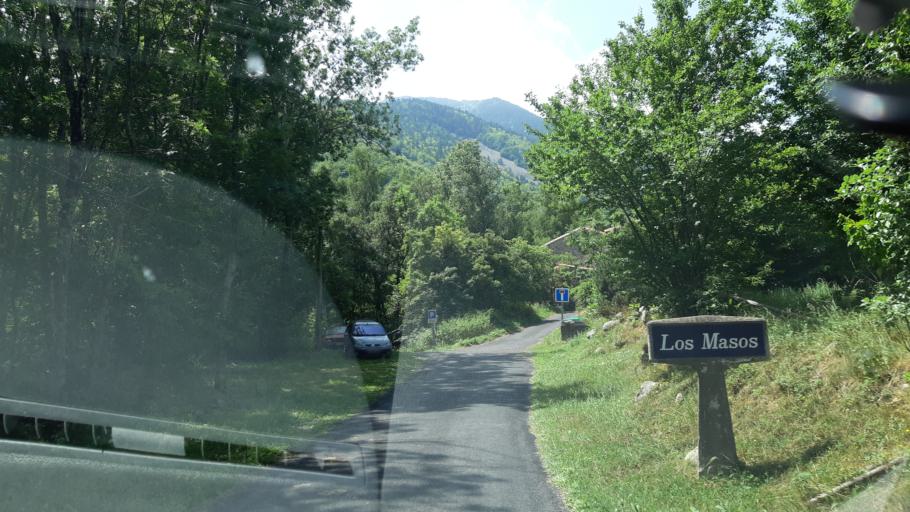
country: FR
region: Languedoc-Roussillon
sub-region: Departement des Pyrenees-Orientales
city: Vinca
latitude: 42.5321
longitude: 2.5200
